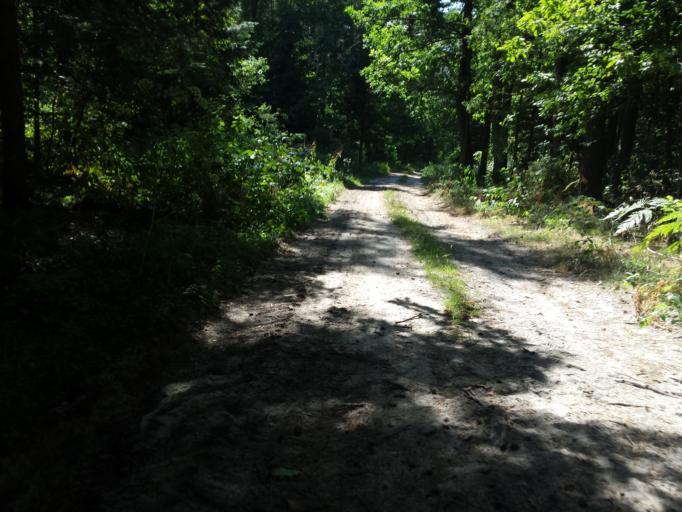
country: PL
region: Swietokrzyskie
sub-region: Powiat kielecki
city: Daleszyce
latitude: 50.8033
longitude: 20.7596
